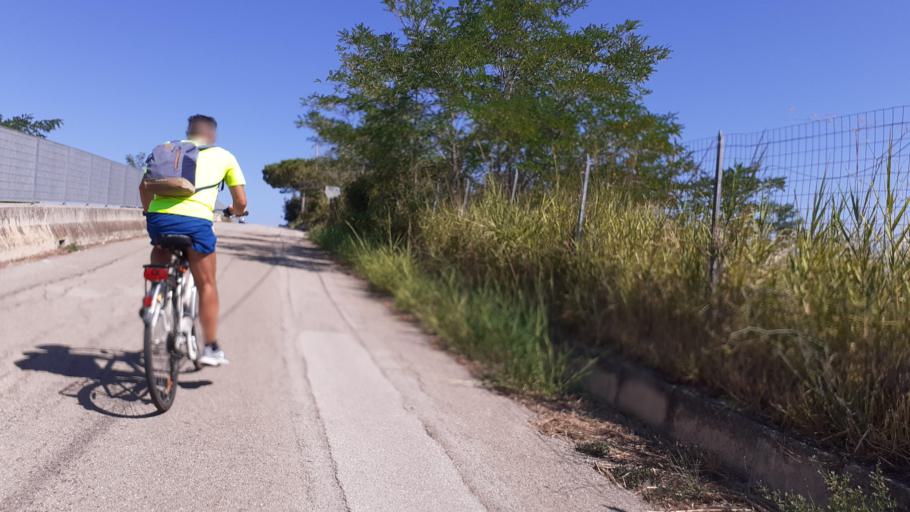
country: IT
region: Abruzzo
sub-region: Provincia di Chieti
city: Vasto
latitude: 42.1503
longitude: 14.7143
